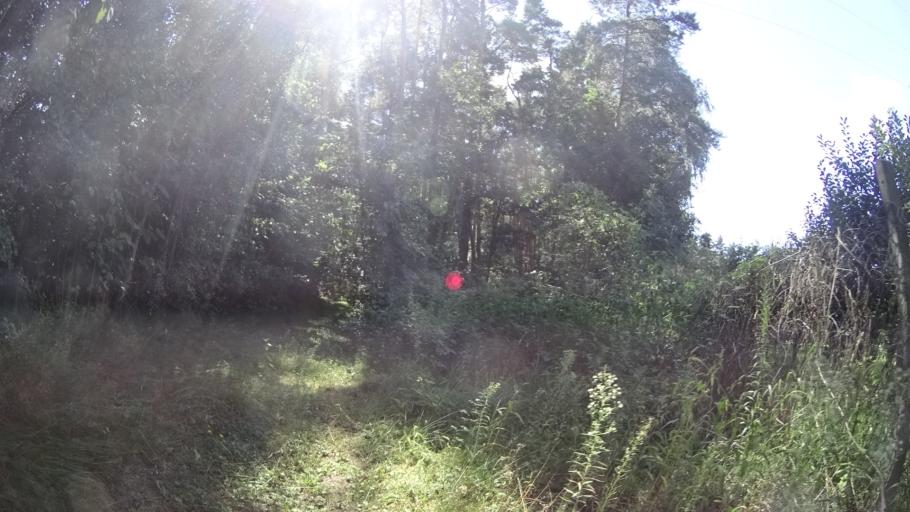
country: PL
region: Masovian Voivodeship
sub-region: Powiat grojecki
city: Mogielnica
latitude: 51.6775
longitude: 20.7512
